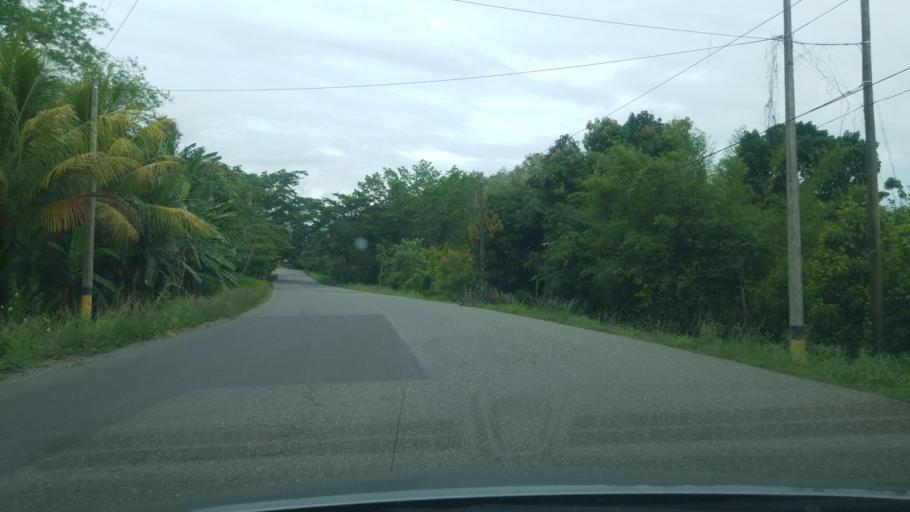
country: HN
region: Santa Barbara
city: La Flecha
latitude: 15.3001
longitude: -88.4794
